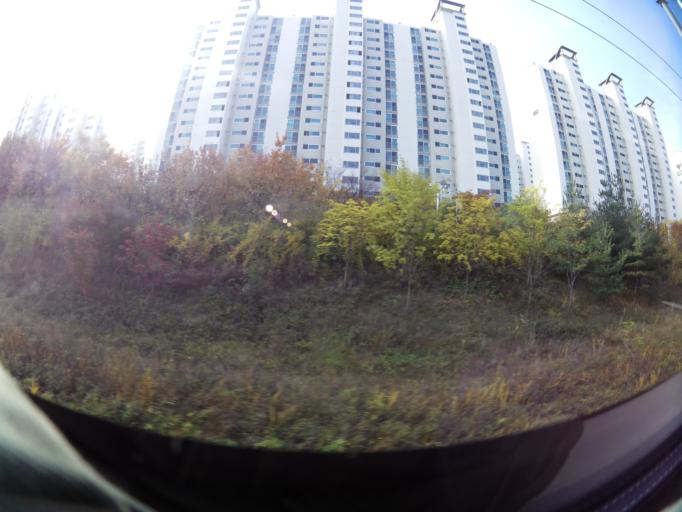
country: KR
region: Gyeongsangbuk-do
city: Gumi
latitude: 36.1244
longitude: 128.3407
